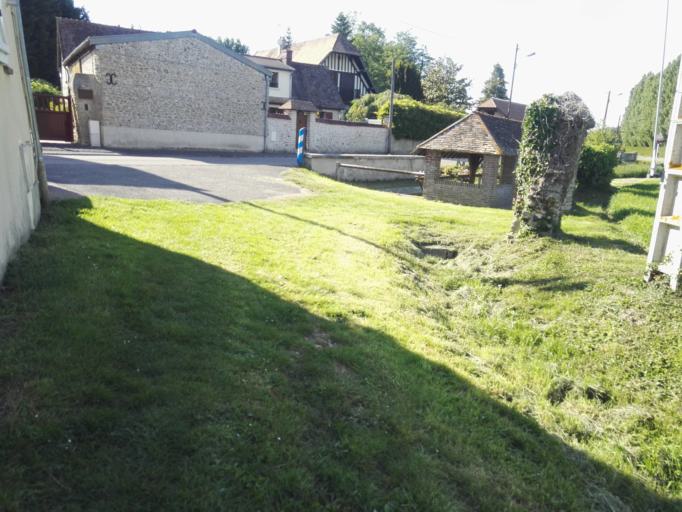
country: FR
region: Haute-Normandie
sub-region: Departement de l'Eure
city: Pacy-sur-Eure
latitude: 48.9977
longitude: 1.3885
